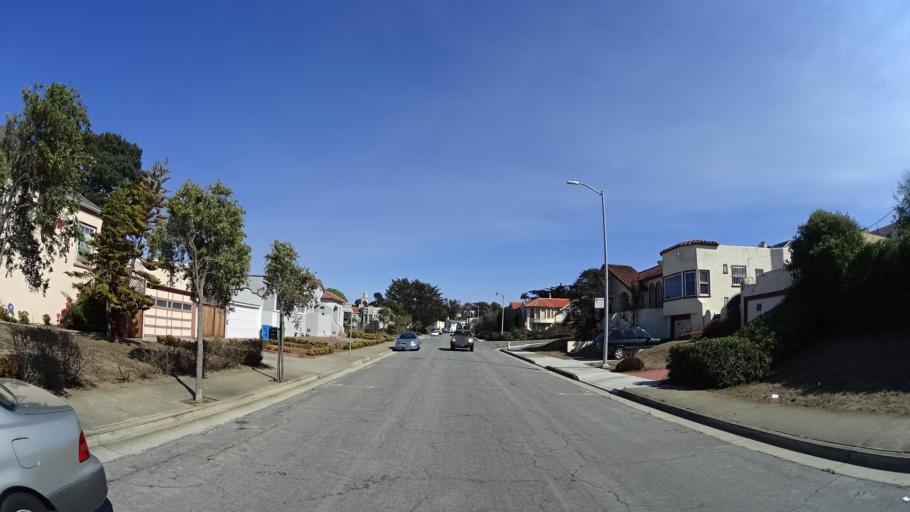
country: US
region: California
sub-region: San Mateo County
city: Daly City
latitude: 37.7236
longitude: -122.4663
